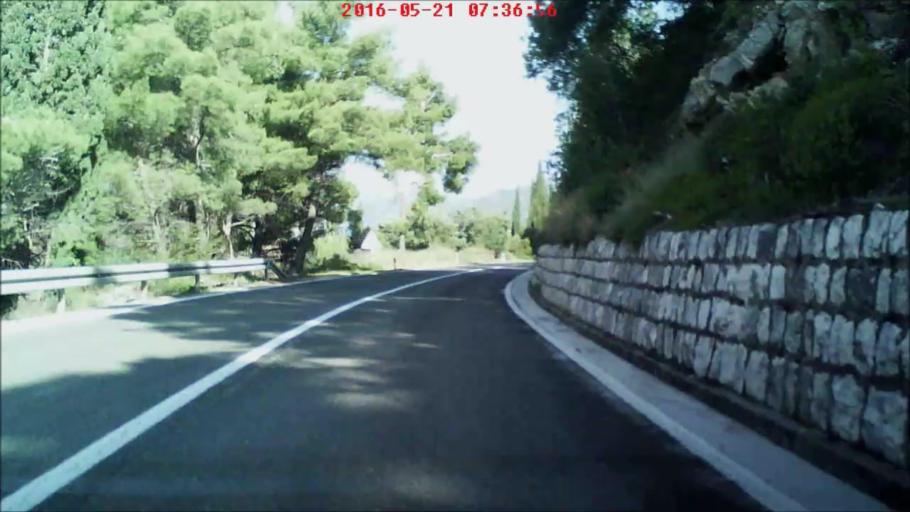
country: HR
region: Dubrovacko-Neretvanska
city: Podgora
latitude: 42.7860
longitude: 17.8589
